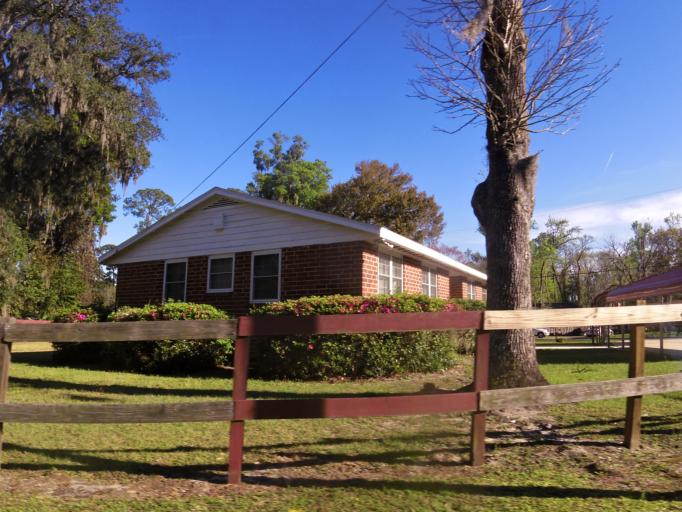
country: US
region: Florida
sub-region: Duval County
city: Jacksonville
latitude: 30.3956
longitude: -81.6783
